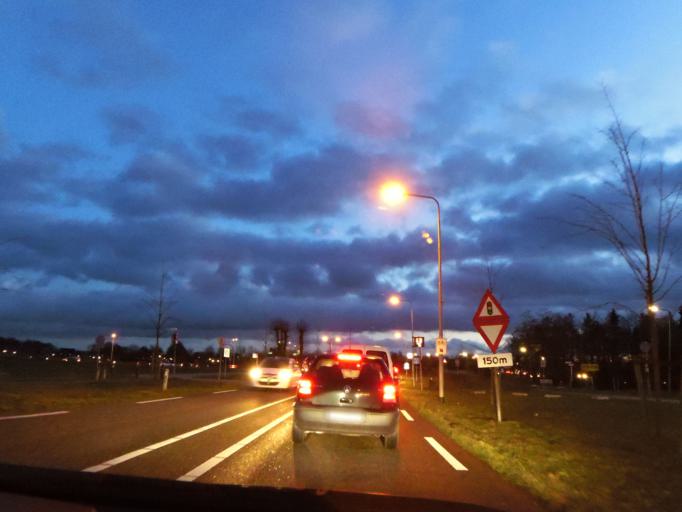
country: NL
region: Limburg
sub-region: Gemeente Roerdalen
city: Melick
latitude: 51.1659
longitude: 6.0071
